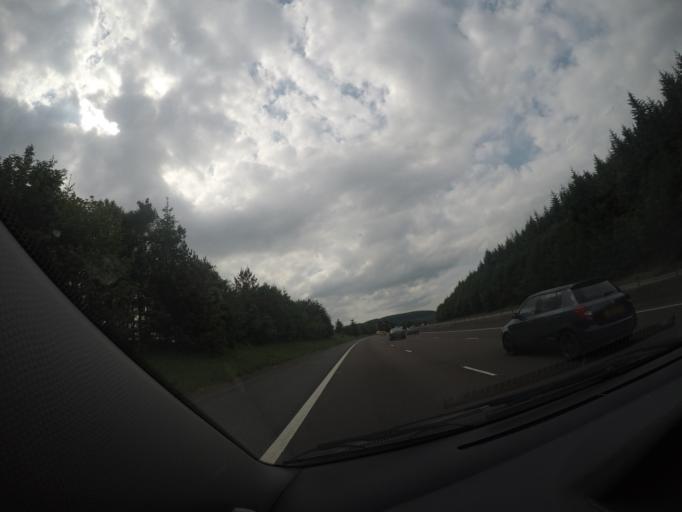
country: GB
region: Scotland
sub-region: Dumfries and Galloway
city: Moffat
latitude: 55.4104
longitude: -3.5727
